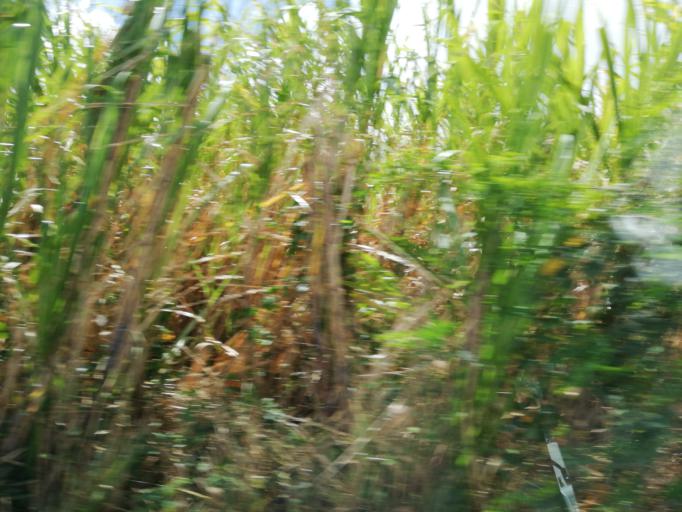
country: MU
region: Riviere du Rempart
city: Esperance Trebuchet
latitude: -20.0719
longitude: 57.6420
